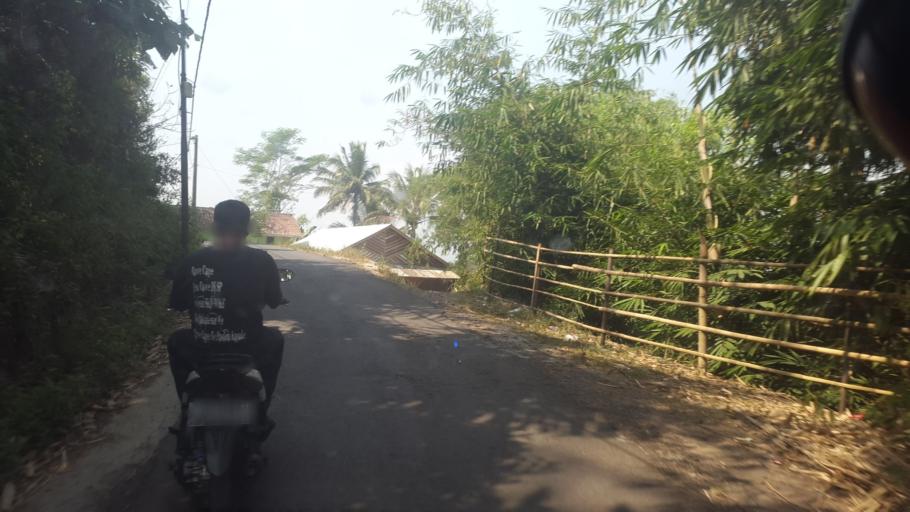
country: ID
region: West Java
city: Pasirreungit
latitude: -6.9312
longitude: 107.0158
